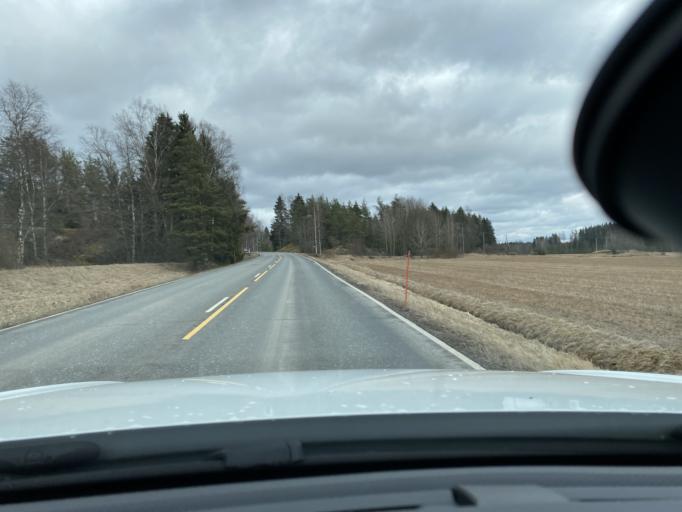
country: FI
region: Pirkanmaa
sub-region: Lounais-Pirkanmaa
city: Punkalaidun
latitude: 61.1034
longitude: 23.1927
